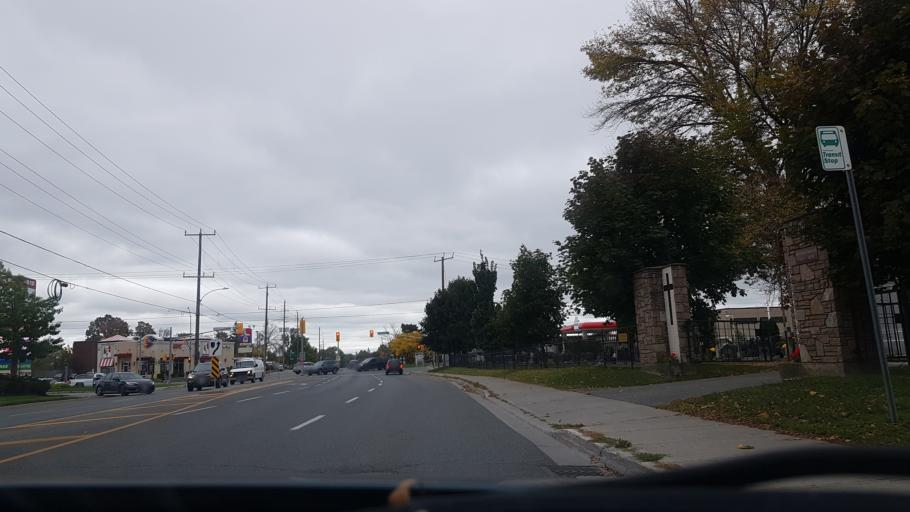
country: CA
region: Ontario
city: Peterborough
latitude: 44.2868
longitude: -78.3303
